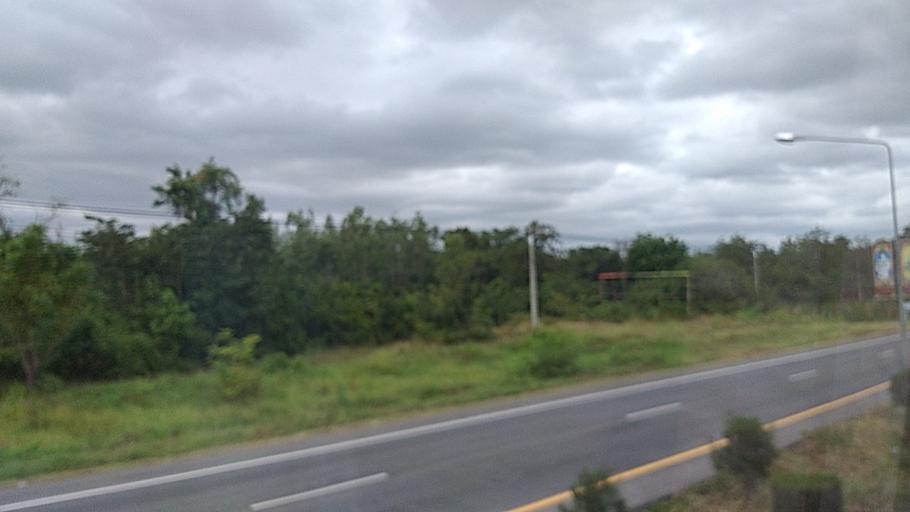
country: TH
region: Khon Kaen
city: Ban Phai
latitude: 16.0200
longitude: 102.7079
